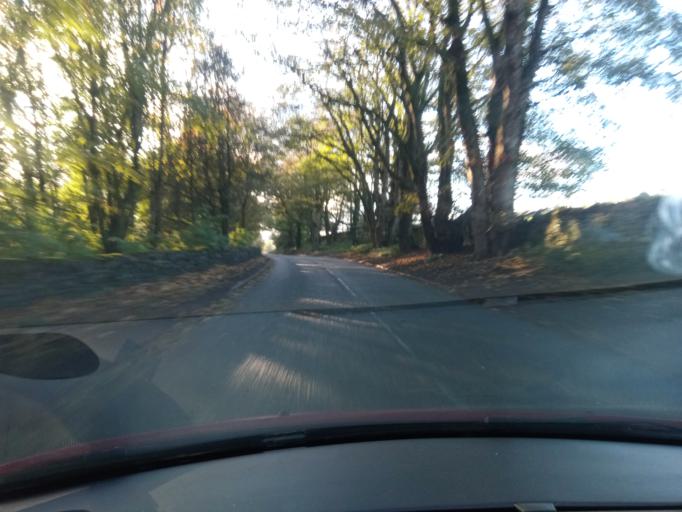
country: GB
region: England
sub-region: County Durham
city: Stanhope
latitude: 54.7420
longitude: -2.0864
